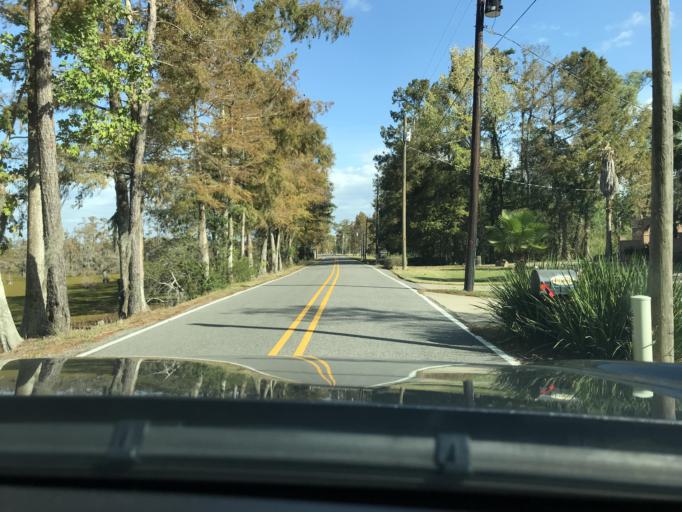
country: US
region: Louisiana
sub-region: Calcasieu Parish
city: Westlake
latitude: 30.3166
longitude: -93.2919
